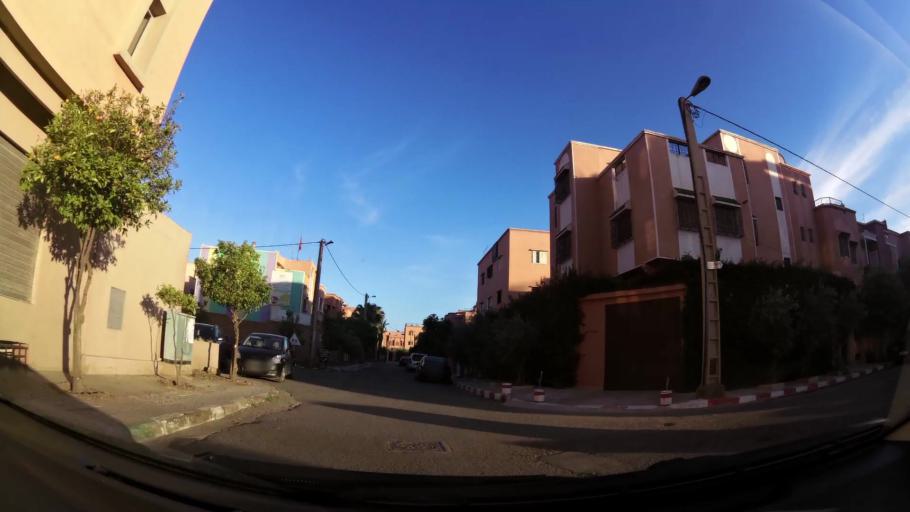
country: MA
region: Marrakech-Tensift-Al Haouz
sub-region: Marrakech
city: Marrakesh
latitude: 31.6230
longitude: -8.0303
